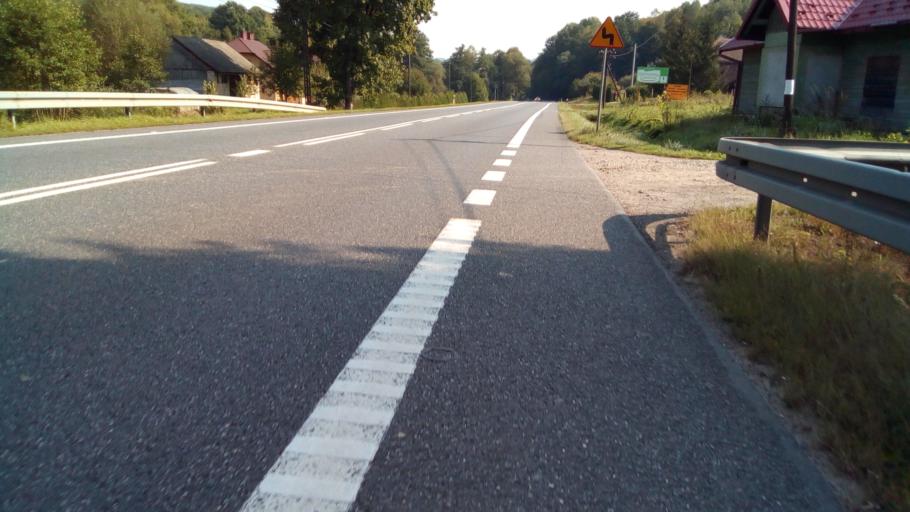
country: PL
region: Subcarpathian Voivodeship
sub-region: Powiat strzyzowski
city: Jawornik
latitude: 49.8172
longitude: 21.8755
